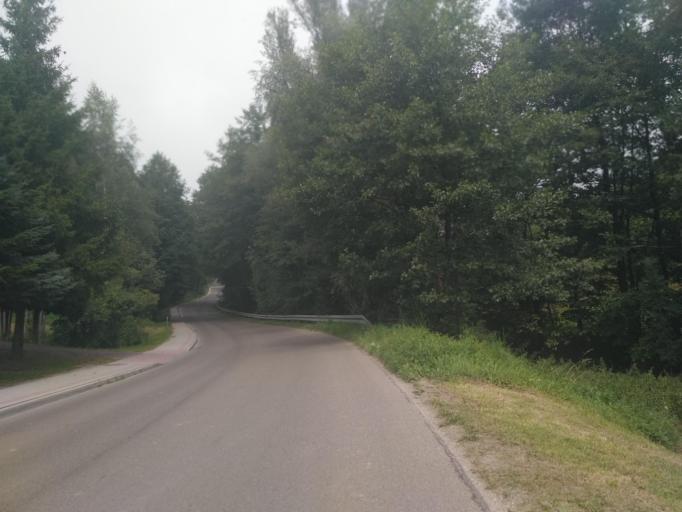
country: PL
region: Subcarpathian Voivodeship
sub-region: Powiat rzeszowski
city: Chmielnik
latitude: 49.9961
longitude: 22.1031
